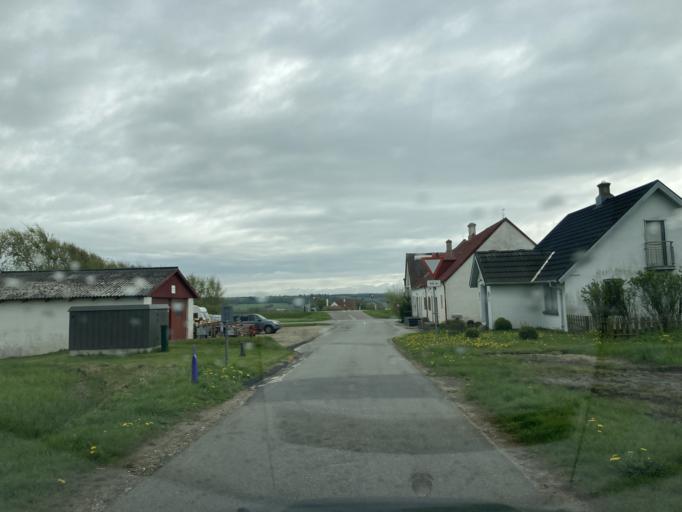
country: DK
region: North Denmark
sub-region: Thisted Kommune
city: Hanstholm
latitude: 57.0116
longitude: 8.5863
